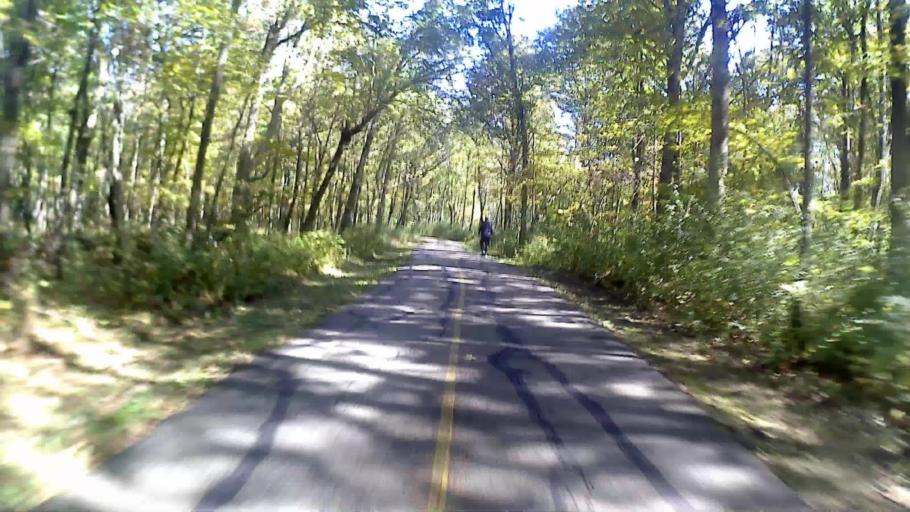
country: US
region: Illinois
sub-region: Cook County
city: Elk Grove Village
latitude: 42.0376
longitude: -87.9917
